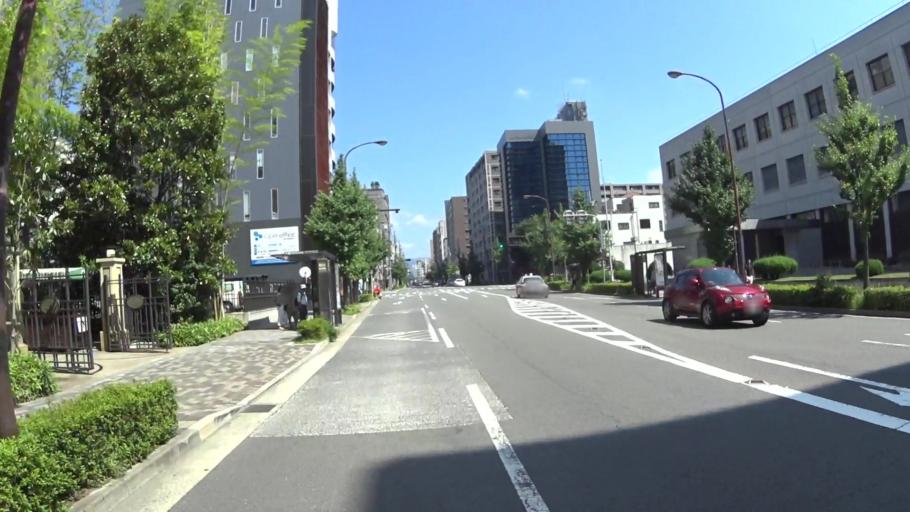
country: JP
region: Kyoto
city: Kyoto
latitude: 35.0119
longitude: 135.7692
